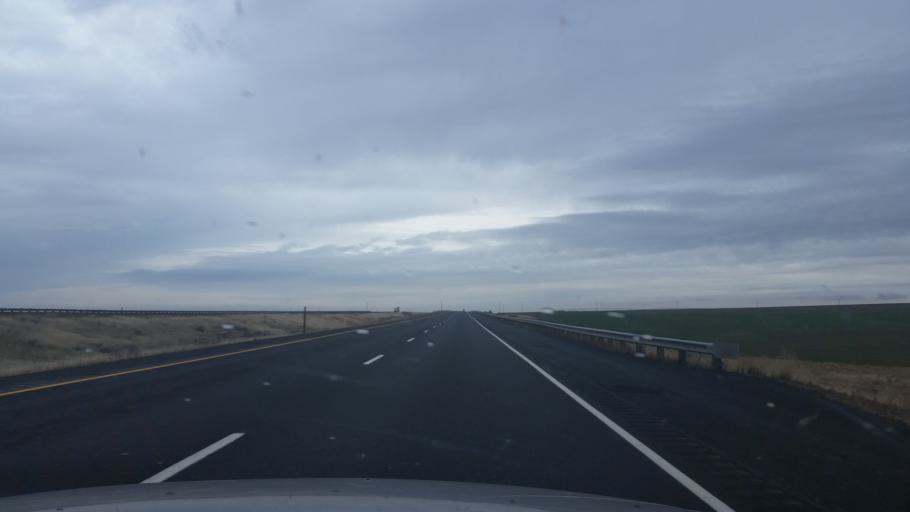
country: US
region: Washington
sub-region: Grant County
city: Warden
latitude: 47.0863
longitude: -118.7998
